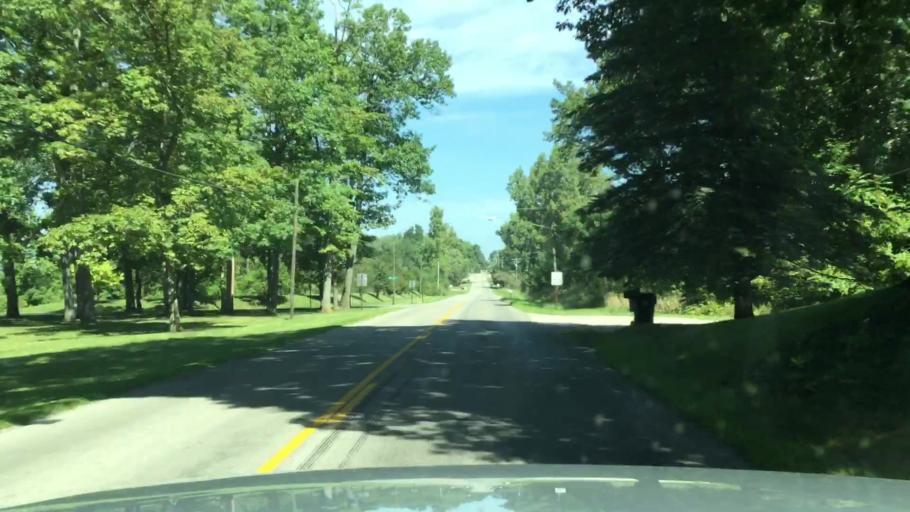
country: US
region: Michigan
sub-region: Lenawee County
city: Manitou Beach-Devils Lake
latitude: 41.9910
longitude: -84.2806
